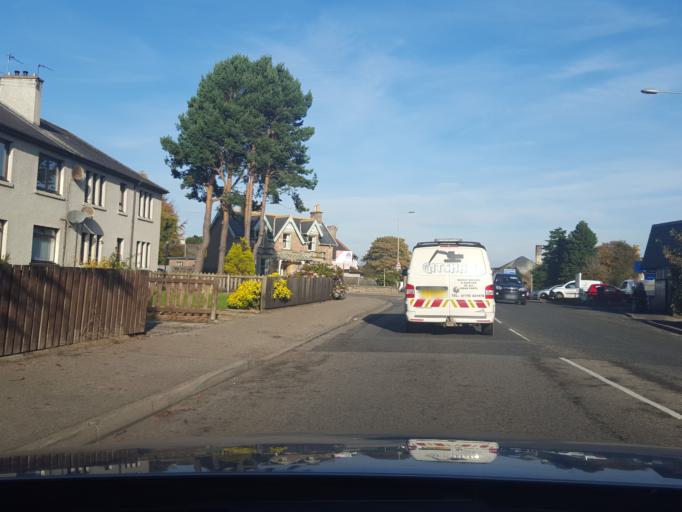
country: GB
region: Scotland
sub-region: Highland
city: Inverness
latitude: 57.4712
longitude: -4.2363
